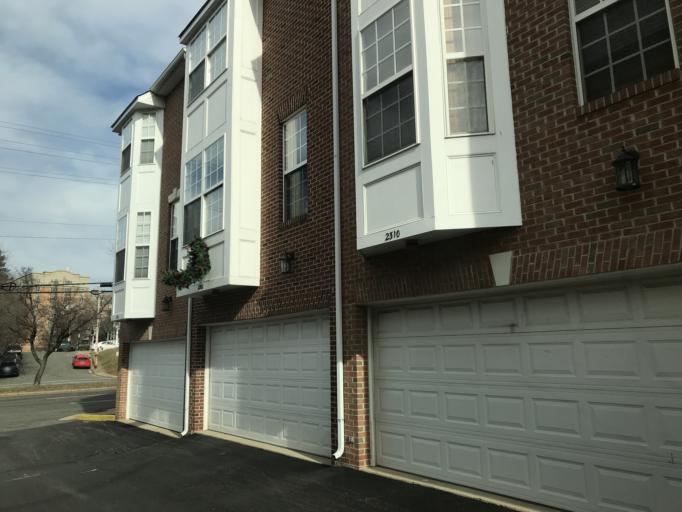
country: US
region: Virginia
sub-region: Arlington County
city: Arlington
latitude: 38.8951
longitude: -77.0881
